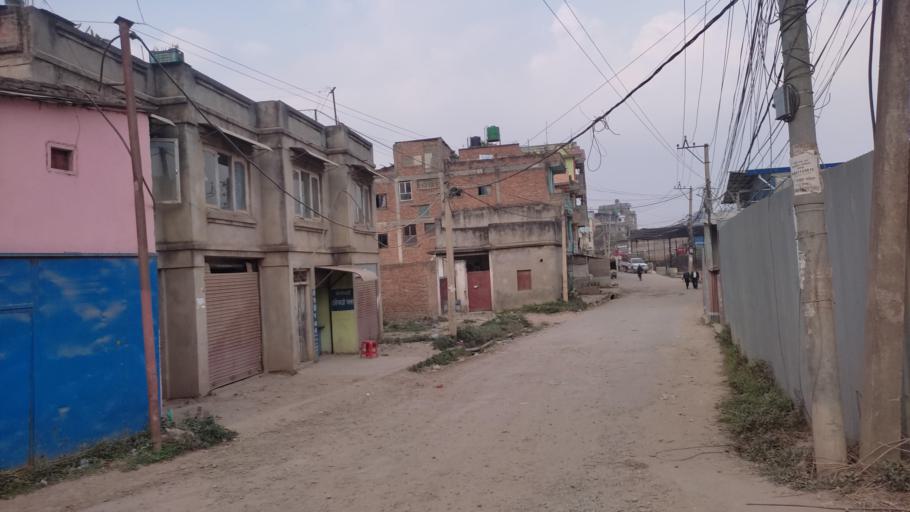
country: NP
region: Central Region
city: Kirtipur
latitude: 27.6821
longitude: 85.2548
